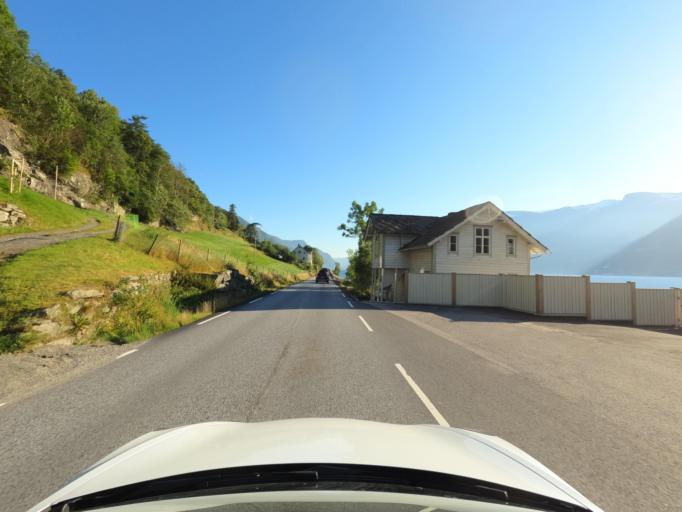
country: NO
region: Hordaland
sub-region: Ullensvang
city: Kinsarvik
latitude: 60.2770
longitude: 6.6190
